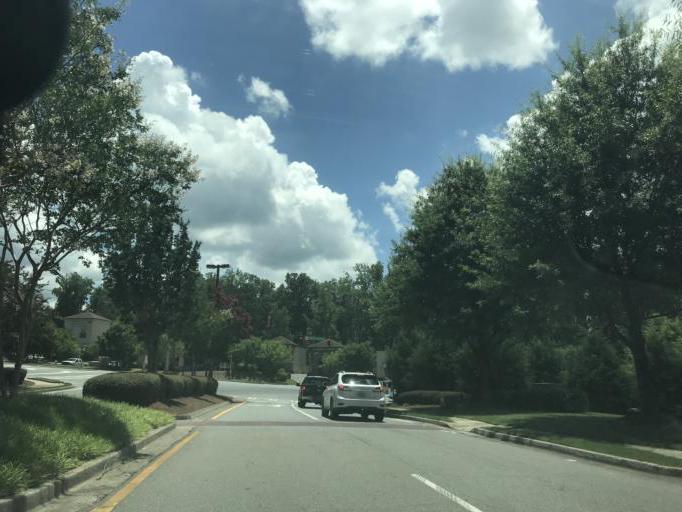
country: US
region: Georgia
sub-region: Fulton County
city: Johns Creek
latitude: 34.0696
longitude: -84.1724
